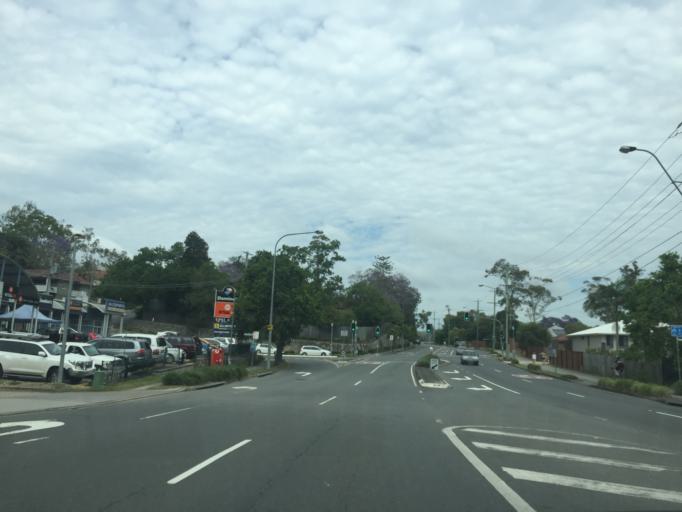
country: AU
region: Queensland
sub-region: Brisbane
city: Toowong
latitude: -27.4464
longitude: 152.9594
